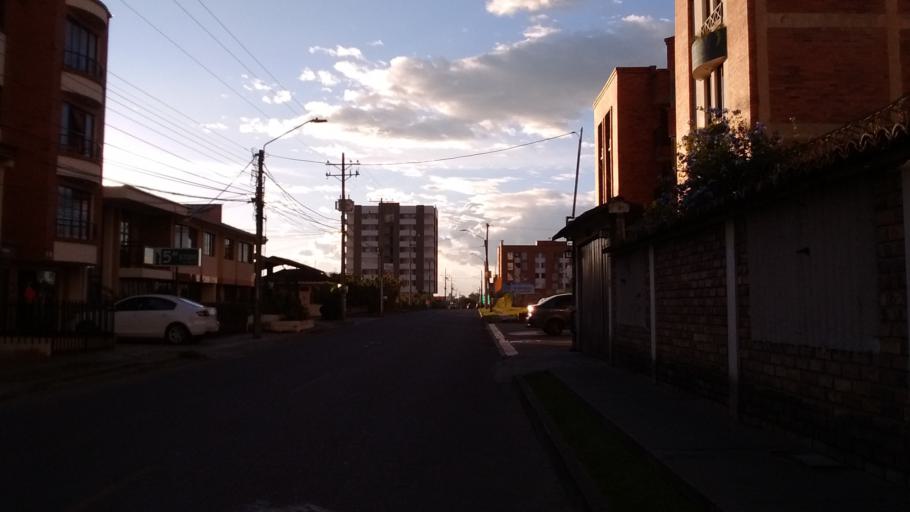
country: CO
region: Cauca
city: Popayan
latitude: 2.4665
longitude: -76.5884
